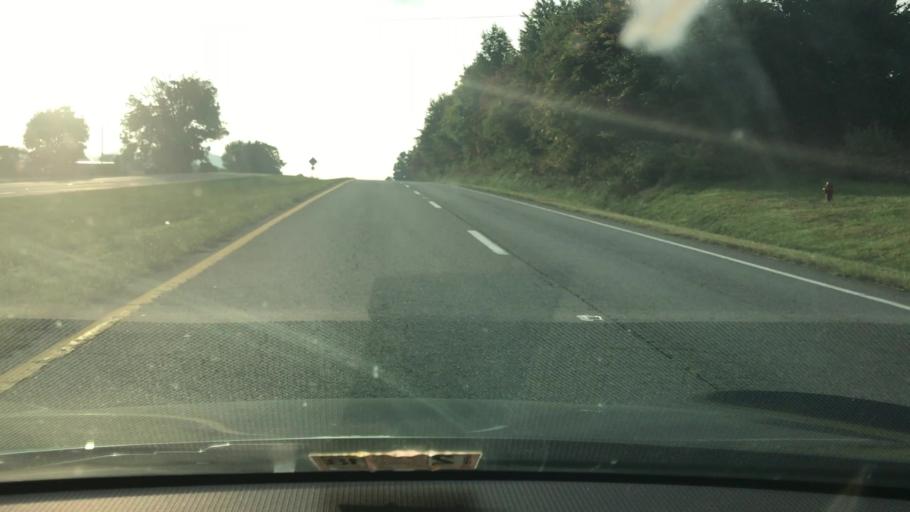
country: US
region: Virginia
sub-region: Botetourt County
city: Blue Ridge
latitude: 37.3814
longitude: -79.7245
